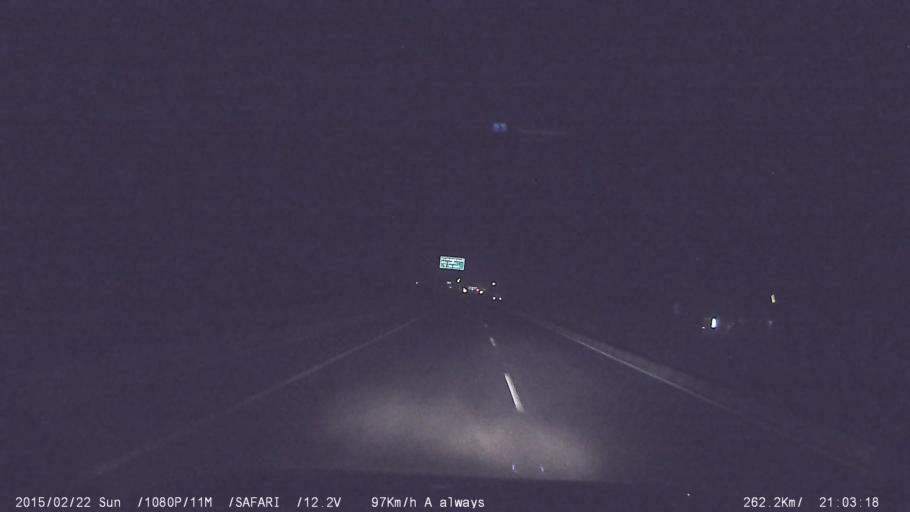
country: IN
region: Tamil Nadu
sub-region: Karur
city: Pallappatti
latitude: 10.6896
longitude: 77.9285
